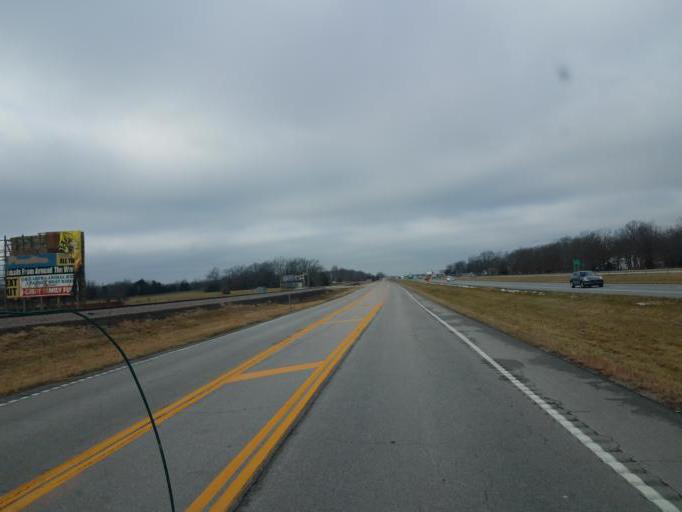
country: US
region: Missouri
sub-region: Greene County
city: Strafford
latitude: 37.2724
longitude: -93.0559
